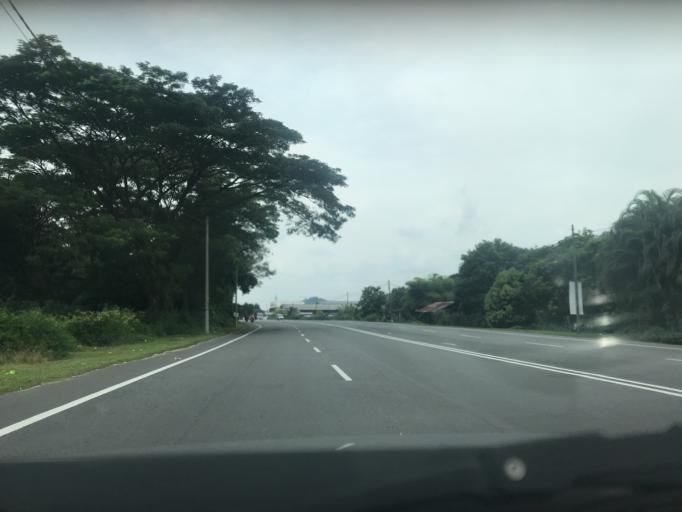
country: MY
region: Perak
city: Ipoh
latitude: 4.6634
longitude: 101.1545
